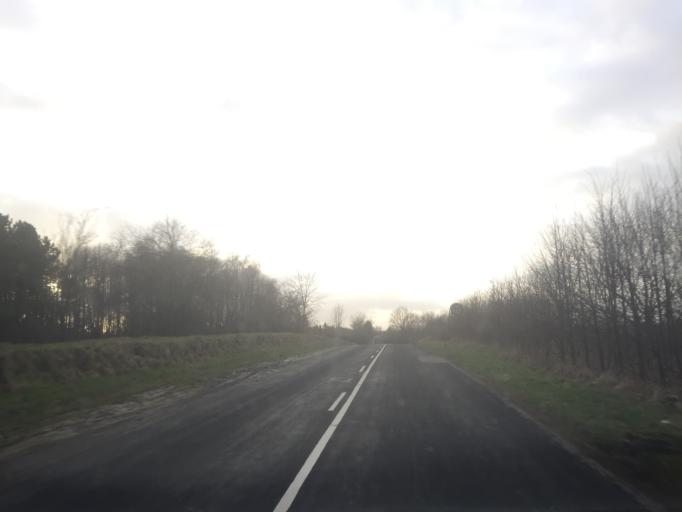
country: DK
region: Capital Region
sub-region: Albertslund Kommune
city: Albertslund
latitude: 55.6890
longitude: 12.3323
